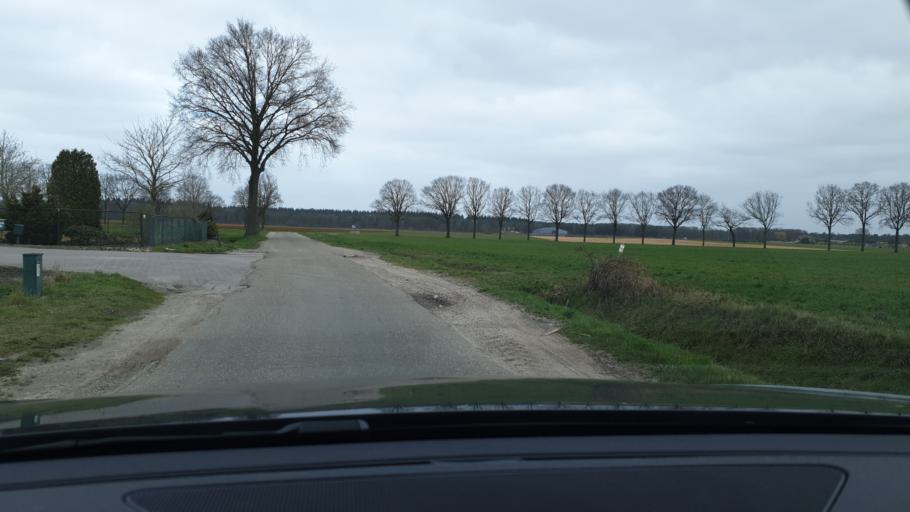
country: NL
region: North Brabant
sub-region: Gemeente Veldhoven
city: Oerle
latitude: 51.4077
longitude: 5.3352
